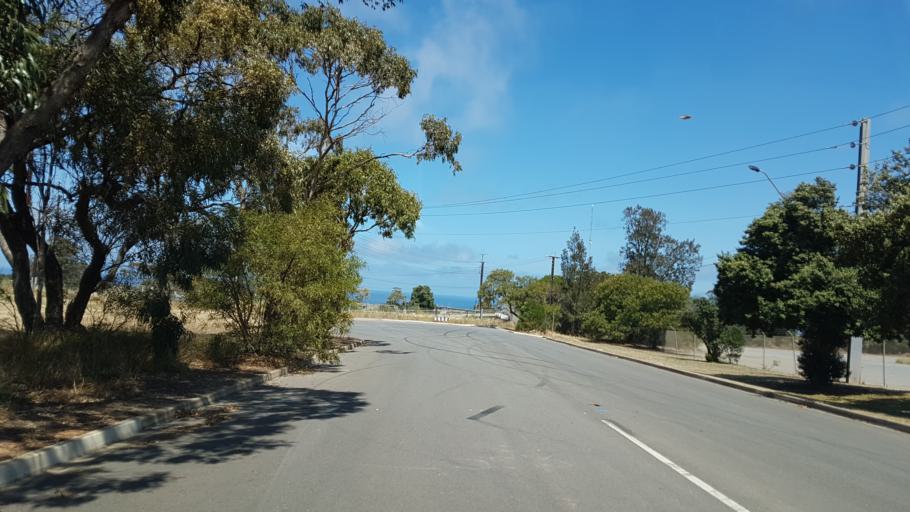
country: AU
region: South Australia
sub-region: Onkaparinga
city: Morphett Vale
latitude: -35.1068
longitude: 138.4916
